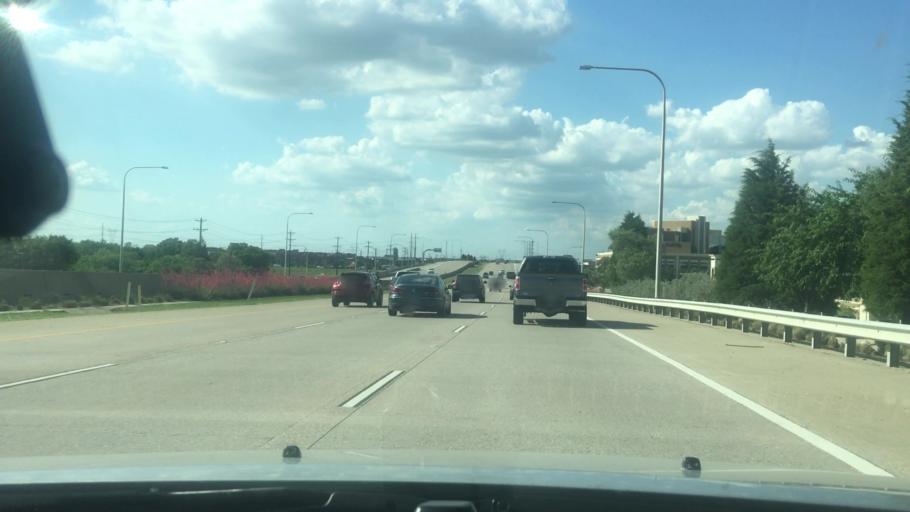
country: US
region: Texas
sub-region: Collin County
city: Frisco
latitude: 33.1471
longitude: -96.8392
